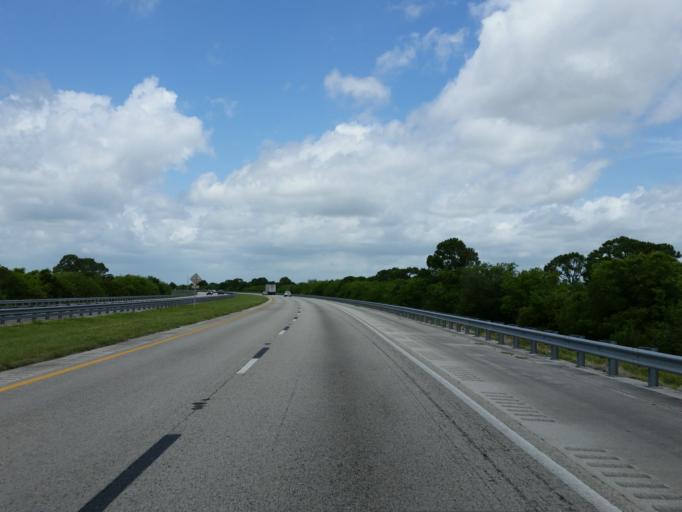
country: US
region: Florida
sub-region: Saint Lucie County
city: Lakewood Park
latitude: 27.4825
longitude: -80.4566
